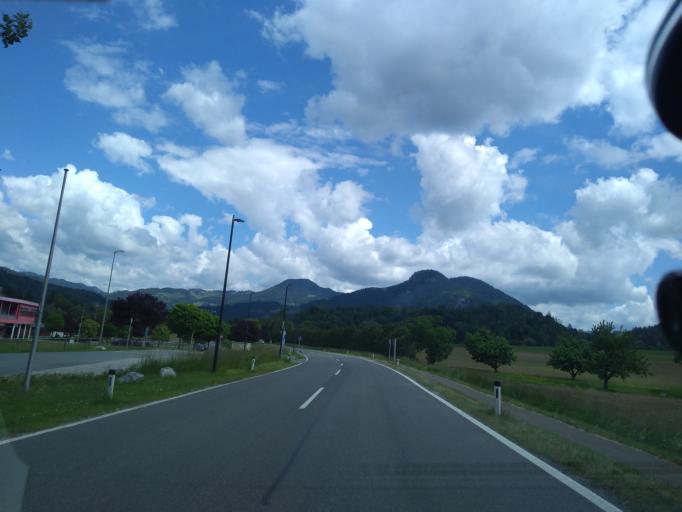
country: AT
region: Styria
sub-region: Politischer Bezirk Graz-Umgebung
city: Frohnleiten
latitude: 47.2549
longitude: 15.3204
